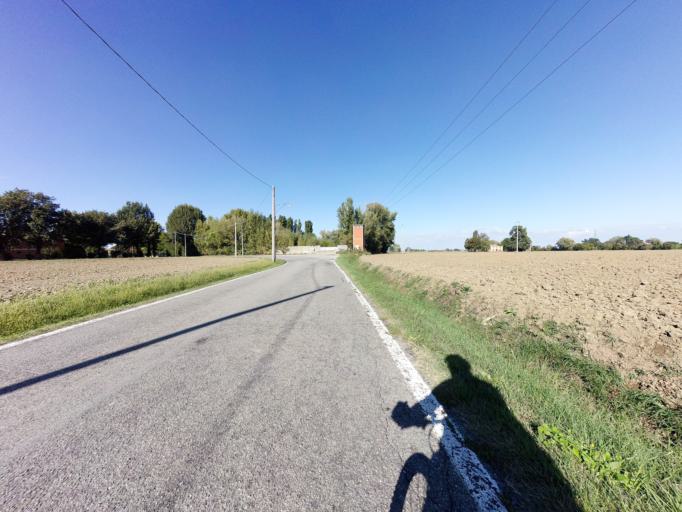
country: IT
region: Emilia-Romagna
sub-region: Provincia di Bologna
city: Progresso
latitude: 44.5637
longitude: 11.3914
